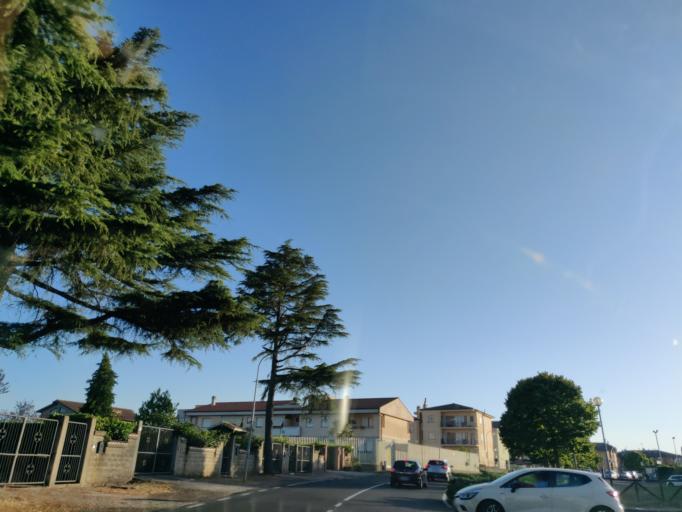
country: IT
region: Latium
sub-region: Provincia di Viterbo
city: Grotte di Castro
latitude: 42.6765
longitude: 11.8671
